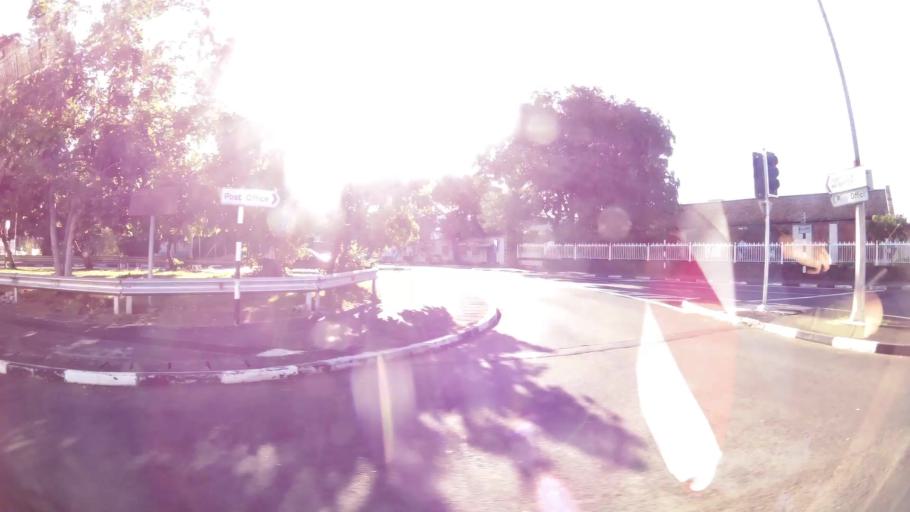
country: MU
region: Port Louis
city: Port Louis
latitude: -20.1590
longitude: 57.5030
